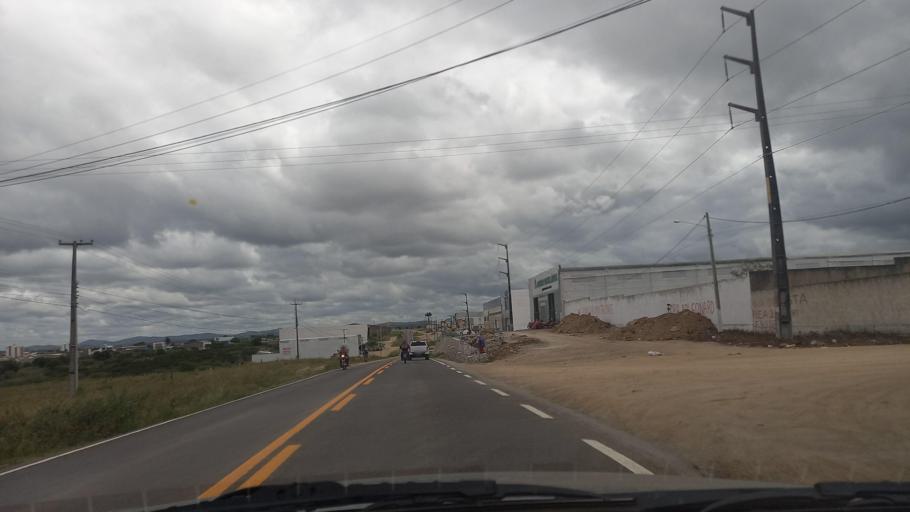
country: BR
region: Pernambuco
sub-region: Caruaru
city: Caruaru
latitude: -8.2545
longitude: -35.9673
